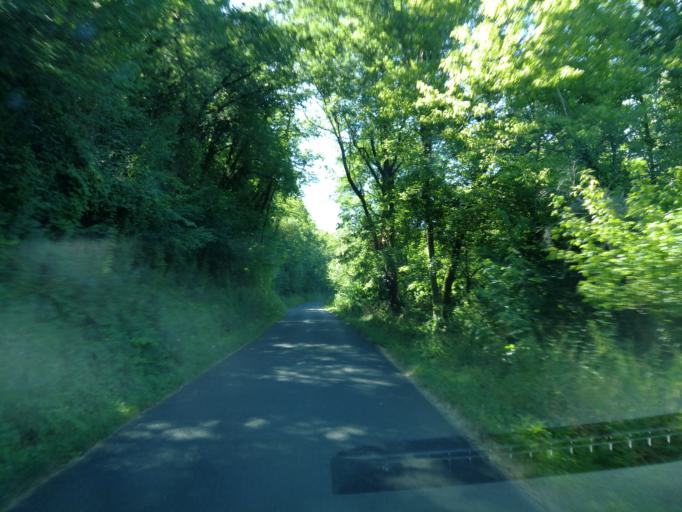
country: FR
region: Midi-Pyrenees
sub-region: Departement du Lot
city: Souillac
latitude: 44.8747
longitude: 1.4047
